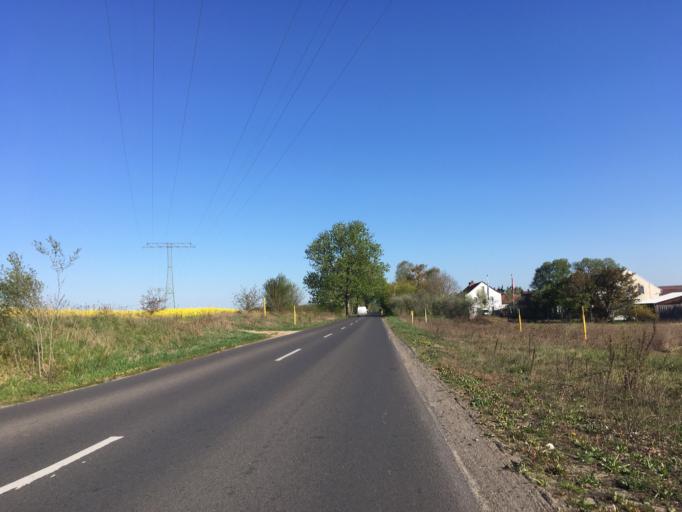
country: DE
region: Brandenburg
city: Bernau bei Berlin
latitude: 52.6836
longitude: 13.5534
